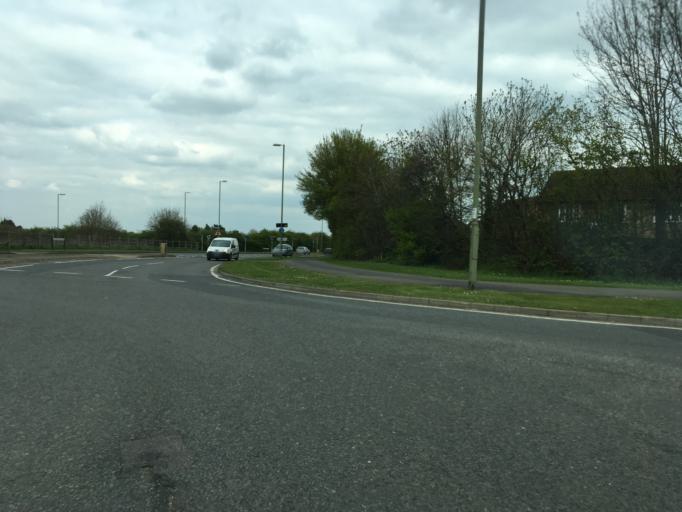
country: GB
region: England
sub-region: Oxfordshire
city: Bicester
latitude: 51.9157
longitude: -1.1557
